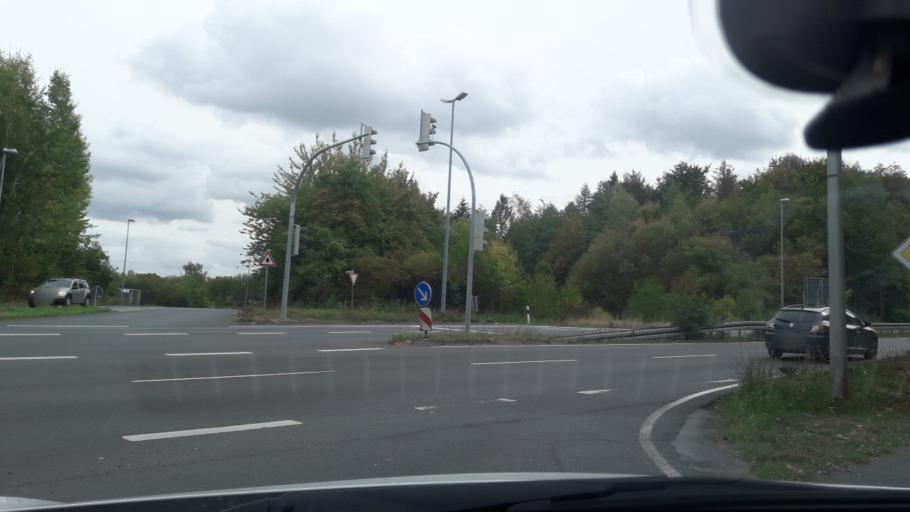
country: DE
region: Lower Saxony
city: Cramme
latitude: 52.0990
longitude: 10.3665
